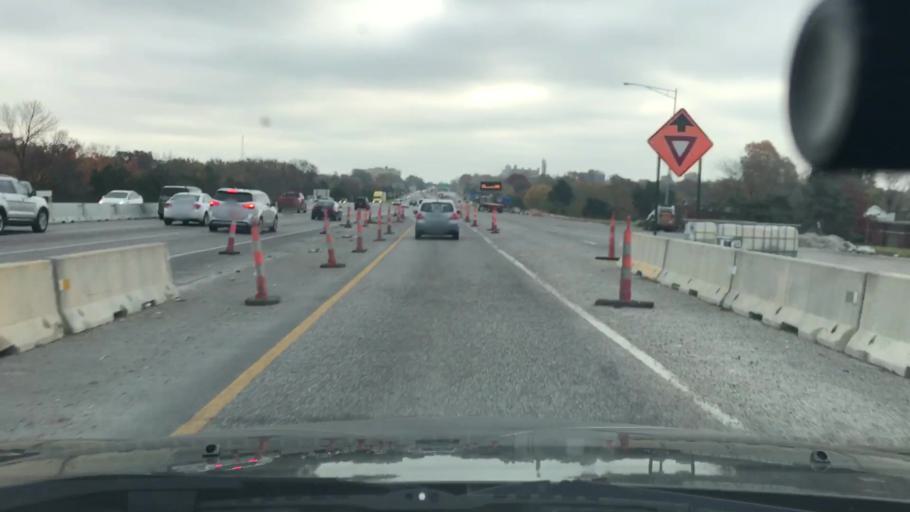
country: US
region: Missouri
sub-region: City of Saint Louis
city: St. Louis
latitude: 38.6181
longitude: -90.2556
